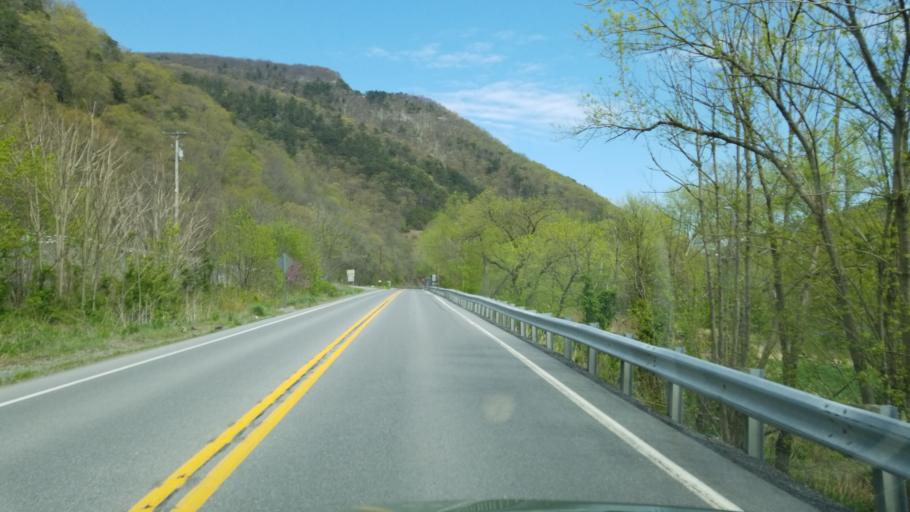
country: US
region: Pennsylvania
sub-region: Huntingdon County
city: Mount Union
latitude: 40.3948
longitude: -77.9272
